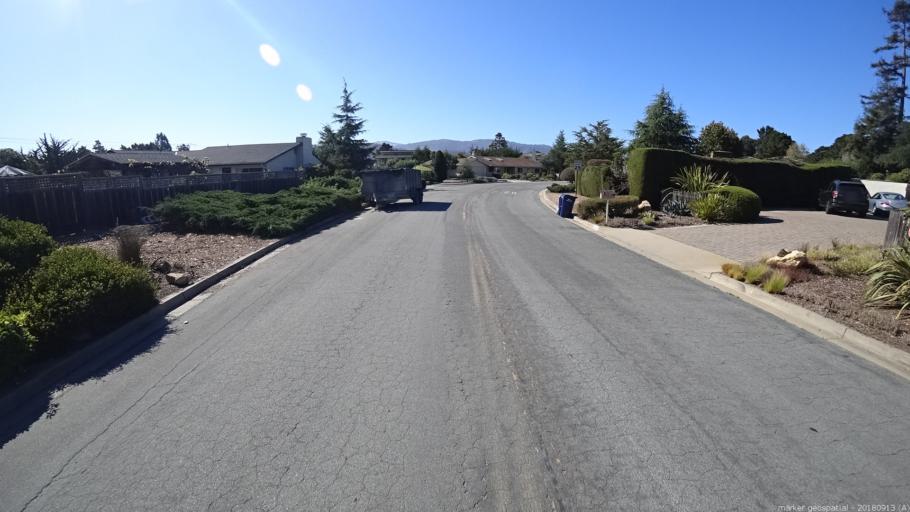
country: US
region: California
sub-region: Monterey County
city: Carmel-by-the-Sea
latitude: 36.5525
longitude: -121.9037
